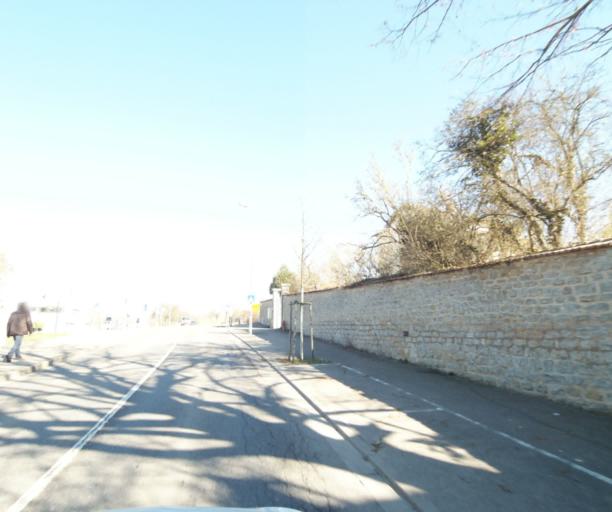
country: FR
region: Lorraine
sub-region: Departement de Meurthe-et-Moselle
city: Malzeville
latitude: 48.7260
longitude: 6.1818
